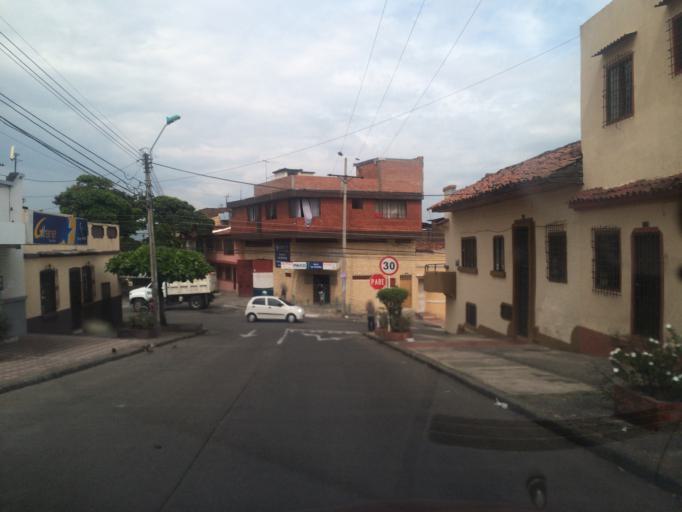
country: CO
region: Valle del Cauca
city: Cali
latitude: 3.4435
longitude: -76.5409
